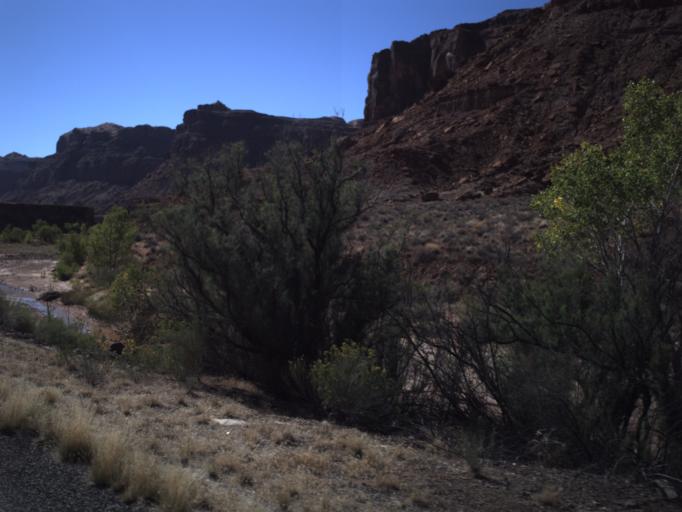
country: US
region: Utah
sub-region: San Juan County
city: Blanding
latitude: 37.9321
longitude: -110.4661
